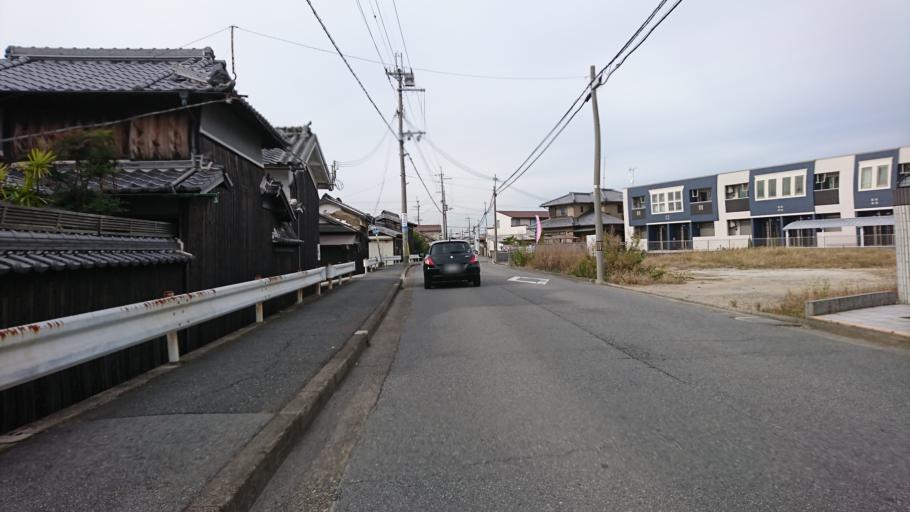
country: JP
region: Hyogo
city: Kakogawacho-honmachi
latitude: 34.7879
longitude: 134.8829
